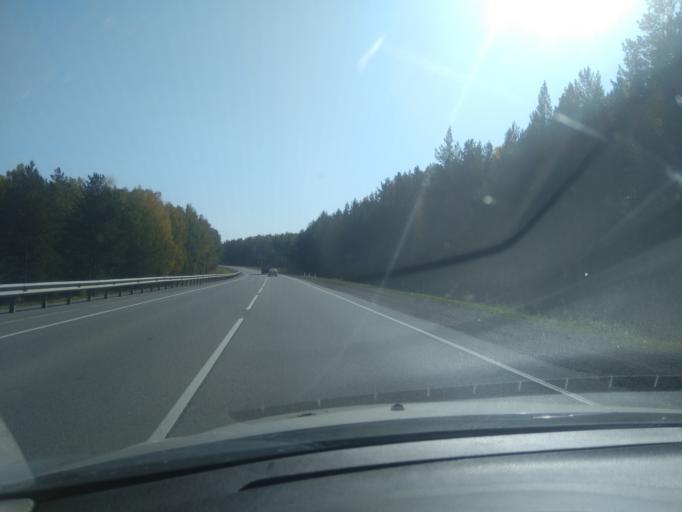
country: RU
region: Sverdlovsk
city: Verkhneye Dubrovo
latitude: 56.7079
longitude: 61.0682
